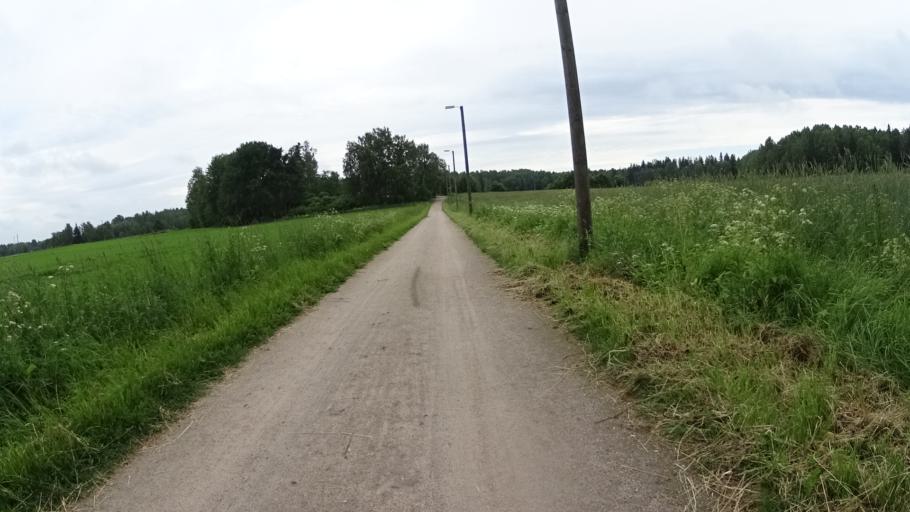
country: FI
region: Uusimaa
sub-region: Helsinki
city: Helsinki
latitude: 60.2658
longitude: 24.9343
